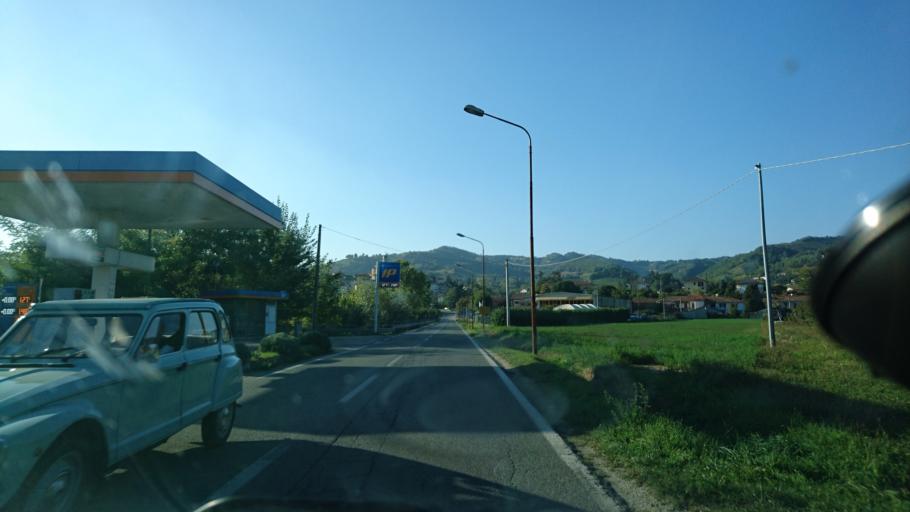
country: IT
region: Piedmont
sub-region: Provincia di Asti
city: Bubbio
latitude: 44.6609
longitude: 8.3027
